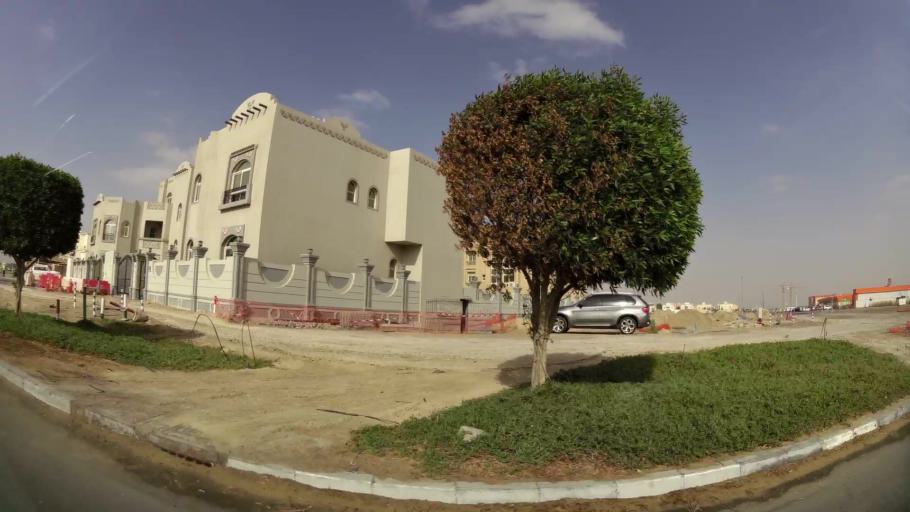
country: AE
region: Abu Dhabi
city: Abu Dhabi
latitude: 24.4009
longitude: 54.5734
